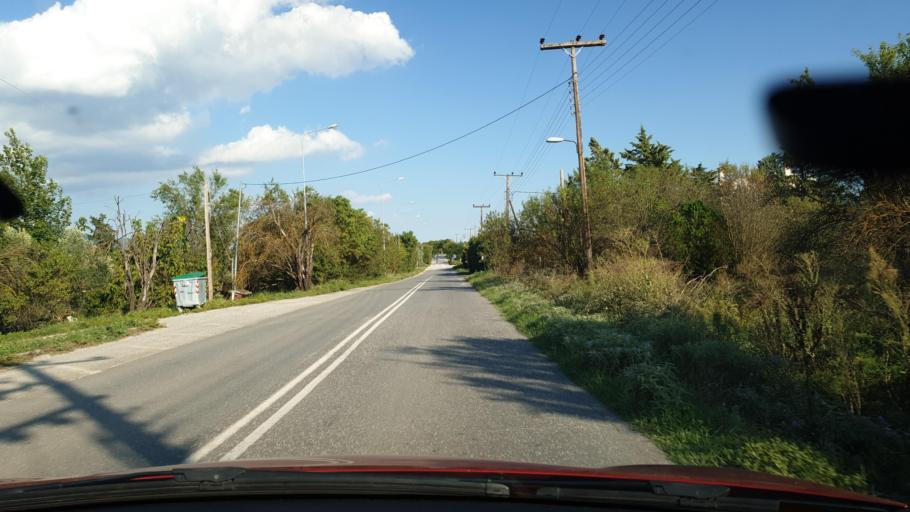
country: GR
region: Central Macedonia
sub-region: Nomos Thessalonikis
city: Souroti
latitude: 40.4785
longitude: 23.0759
